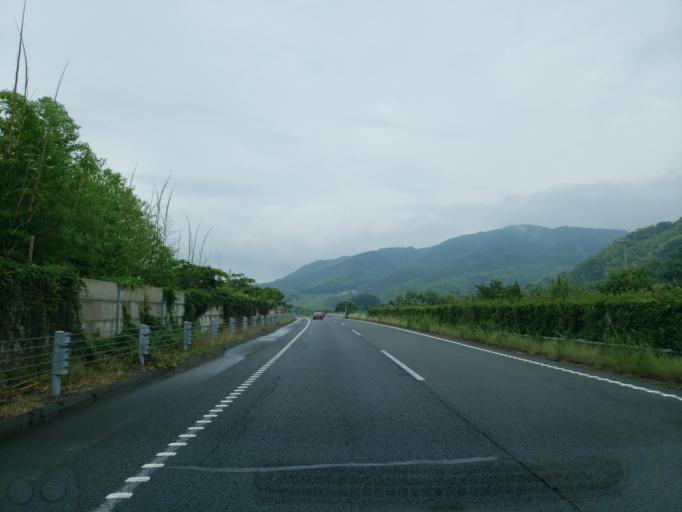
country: JP
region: Hyogo
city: Sumoto
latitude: 34.3953
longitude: 134.8600
